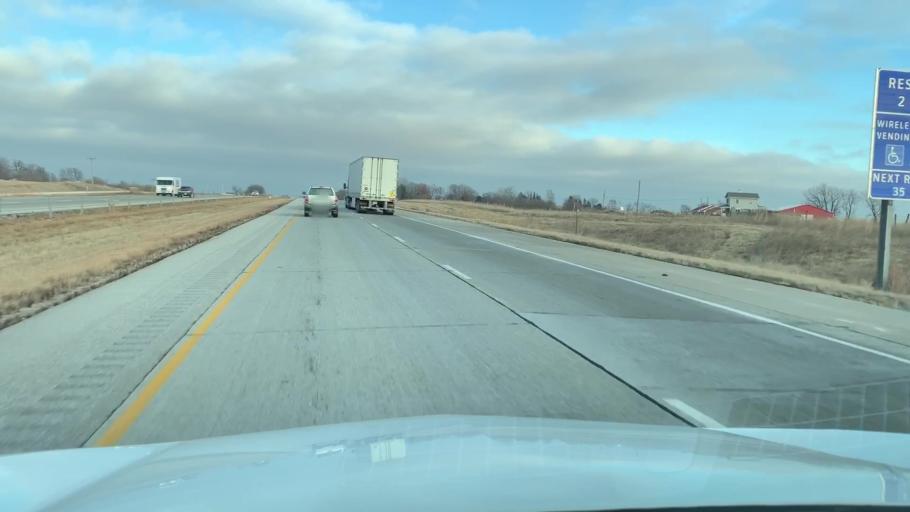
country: US
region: Iowa
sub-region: Polk County
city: Bondurant
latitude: 41.6736
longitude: -93.4330
